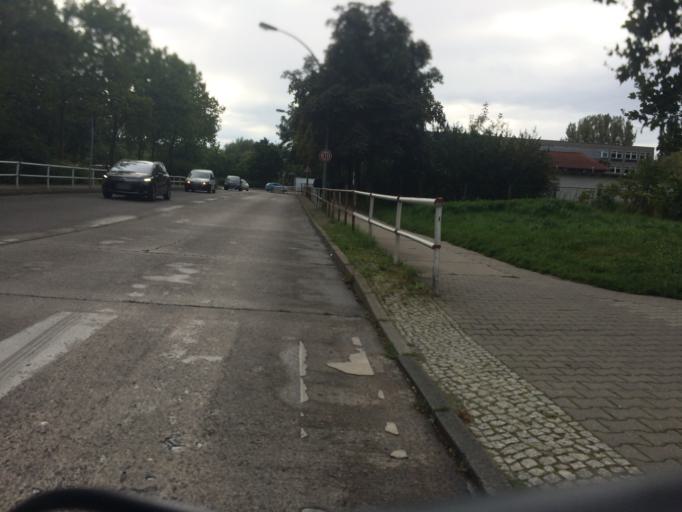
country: DE
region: Berlin
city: Neu-Hohenschoenhausen
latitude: 52.5690
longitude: 13.4945
